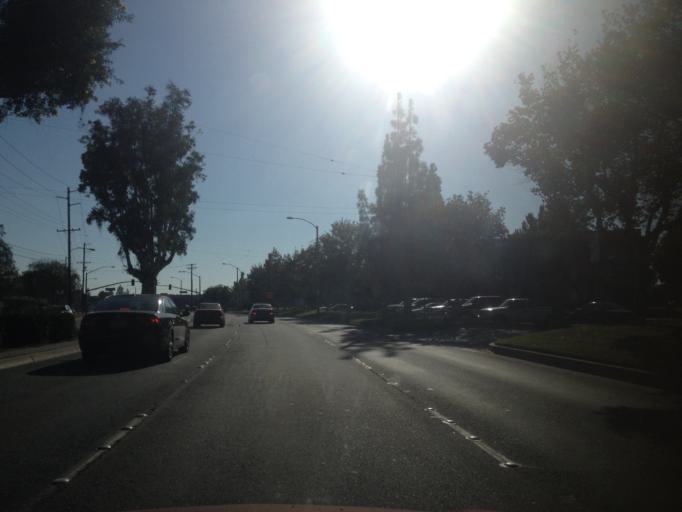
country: US
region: California
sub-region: Orange County
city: Yorba Linda
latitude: 33.8592
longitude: -117.8293
